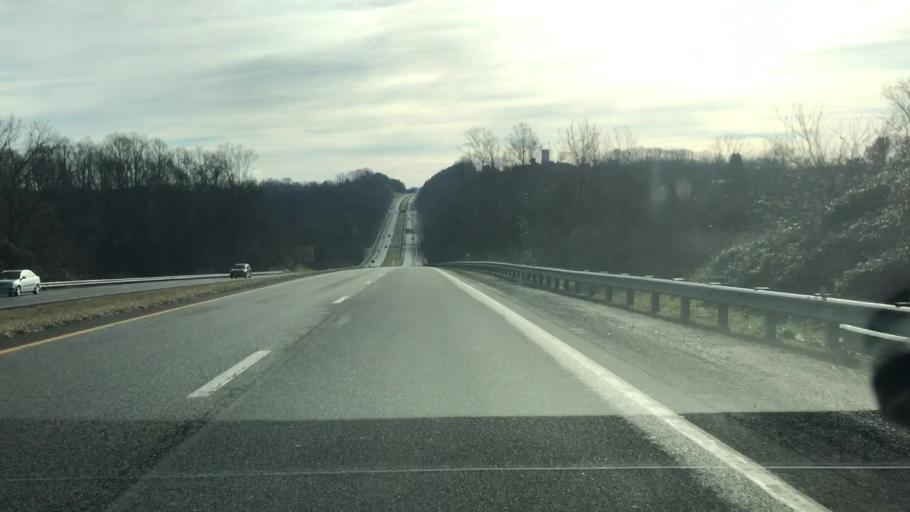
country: US
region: Virginia
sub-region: Montgomery County
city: Christiansburg
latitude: 37.1474
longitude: -80.3951
